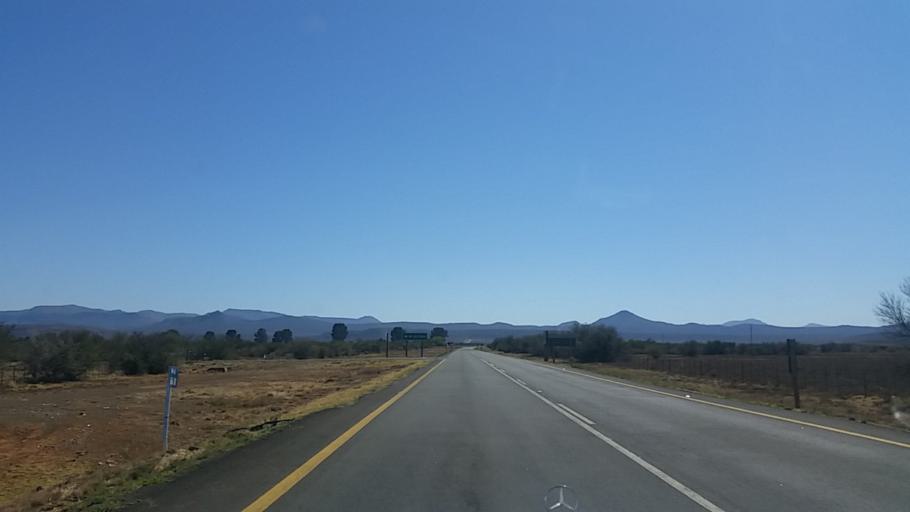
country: ZA
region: Eastern Cape
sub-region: Cacadu District Municipality
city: Graaff-Reinet
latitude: -32.1991
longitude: 24.5533
